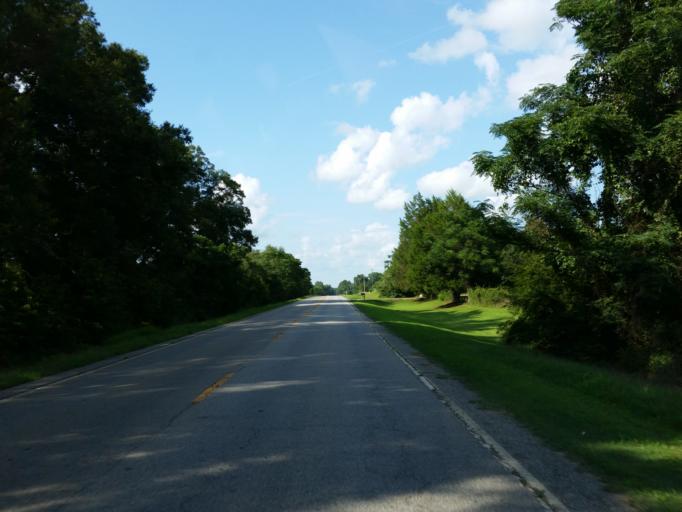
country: US
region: Georgia
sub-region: Lee County
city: Leesburg
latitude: 31.8301
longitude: -84.1023
